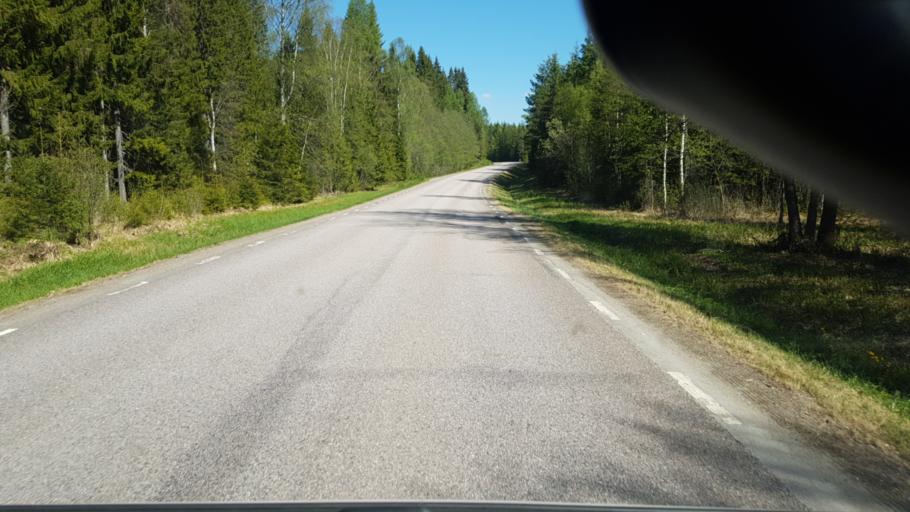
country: SE
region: Vaermland
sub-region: Eda Kommun
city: Charlottenberg
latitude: 59.8707
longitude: 12.4142
